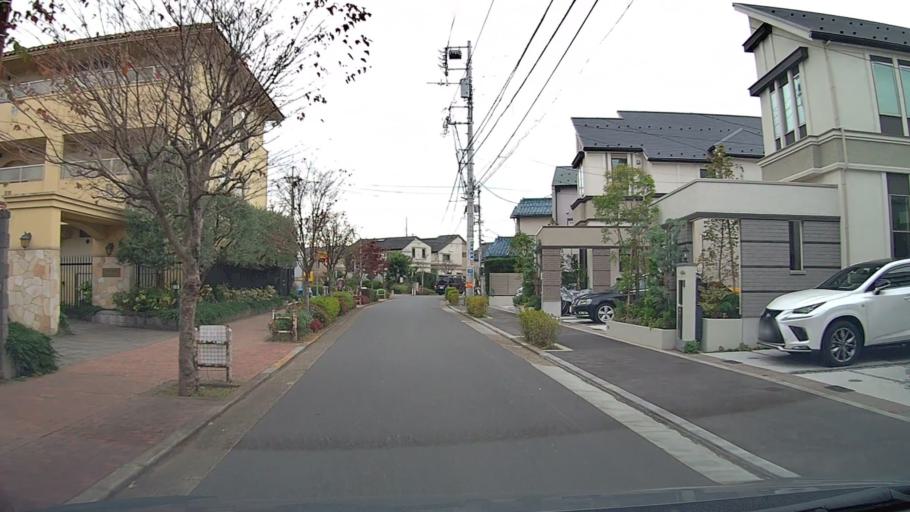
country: JP
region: Saitama
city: Wako
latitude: 35.7320
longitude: 139.6312
